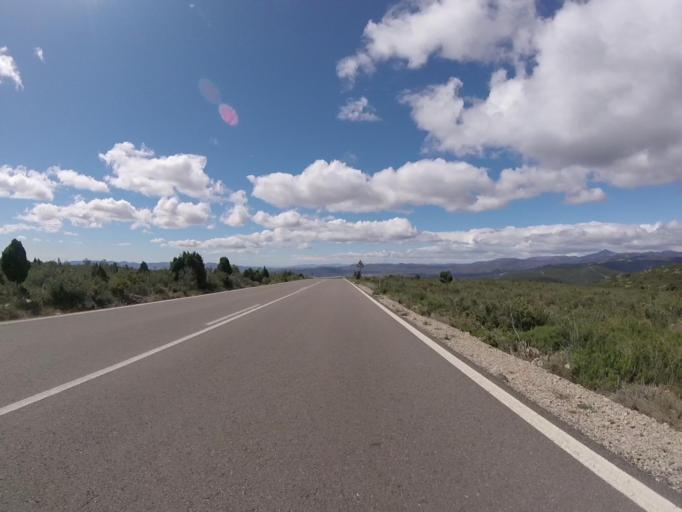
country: ES
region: Valencia
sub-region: Provincia de Castello
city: Culla
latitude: 40.3021
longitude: -0.1266
